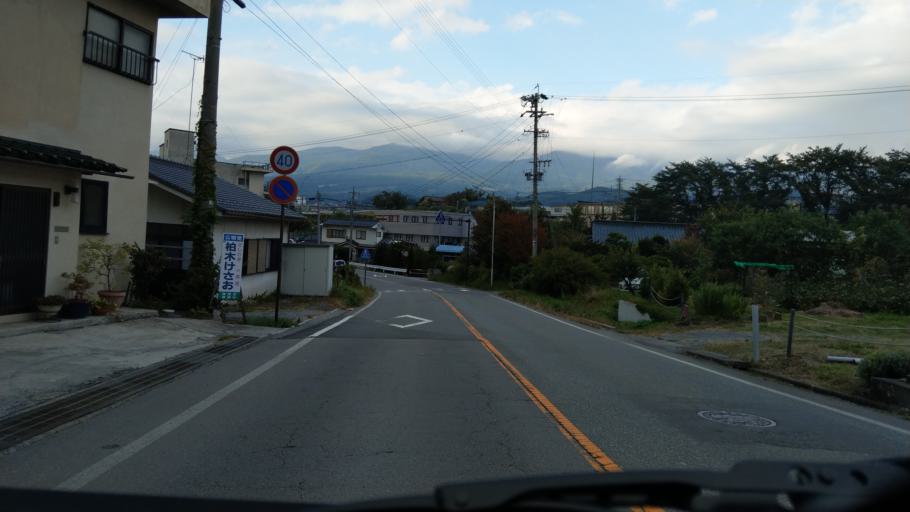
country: JP
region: Nagano
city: Komoro
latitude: 36.3159
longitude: 138.4318
